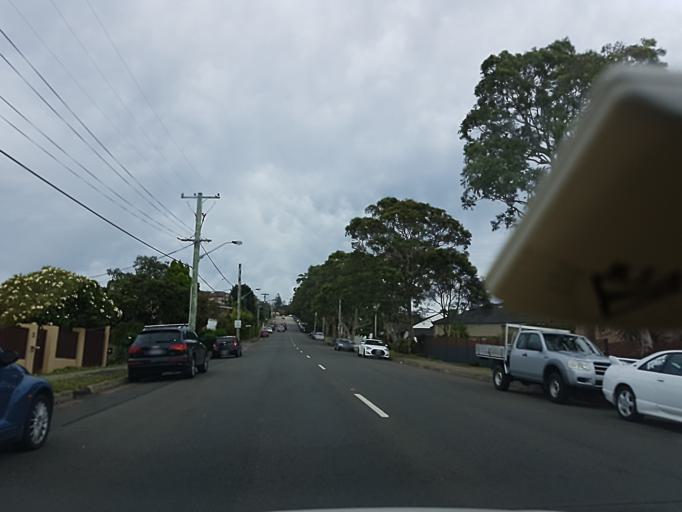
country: AU
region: New South Wales
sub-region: Warringah
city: Brookvale
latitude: -33.7602
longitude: 151.2676
